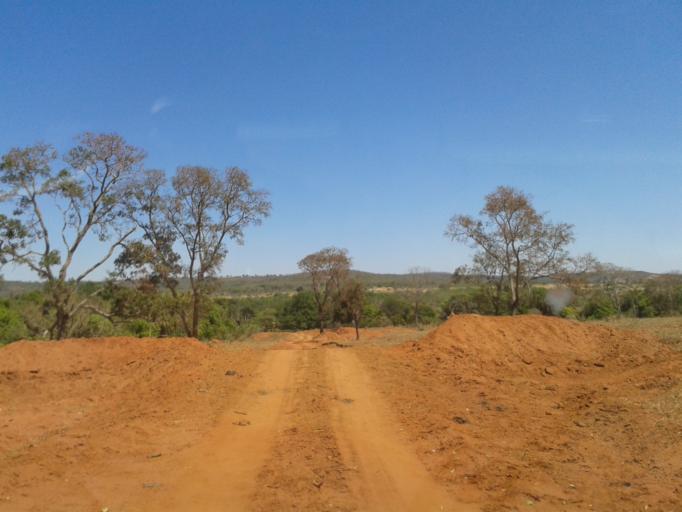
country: BR
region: Minas Gerais
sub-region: Ituiutaba
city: Ituiutaba
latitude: -19.1101
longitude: -49.2728
